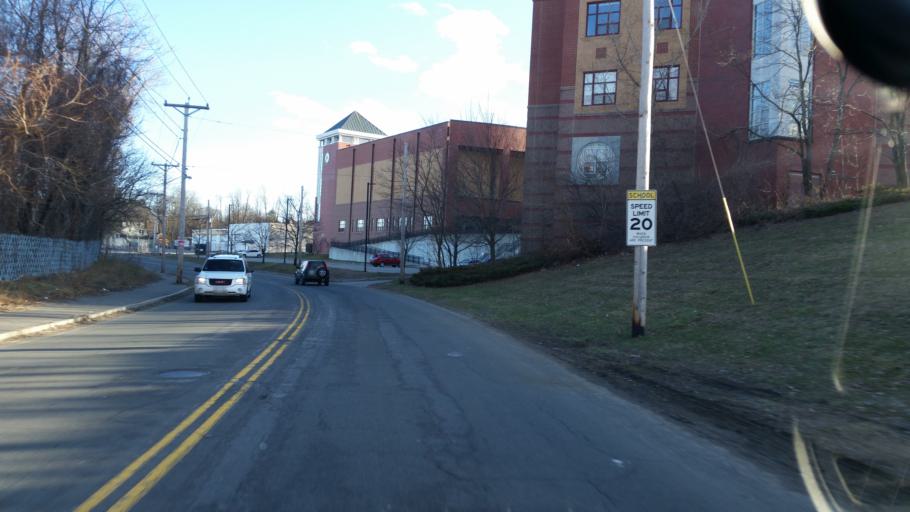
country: US
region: Massachusetts
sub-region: Essex County
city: North Andover
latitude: 42.7194
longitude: -71.1425
